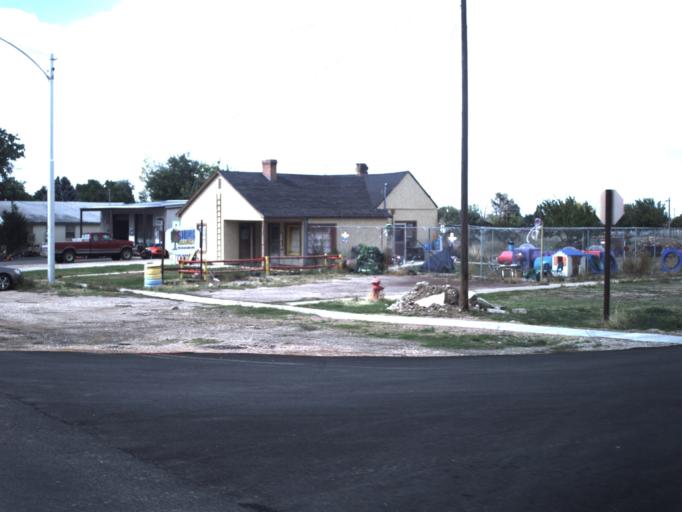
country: US
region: Utah
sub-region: Millard County
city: Fillmore
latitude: 38.9580
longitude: -112.3264
